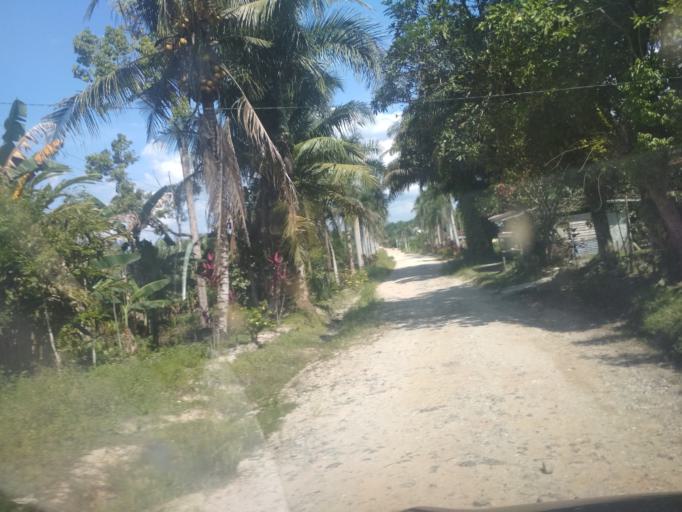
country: ID
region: West Kalimantan
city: Tayan
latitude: 0.3462
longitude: 109.9208
